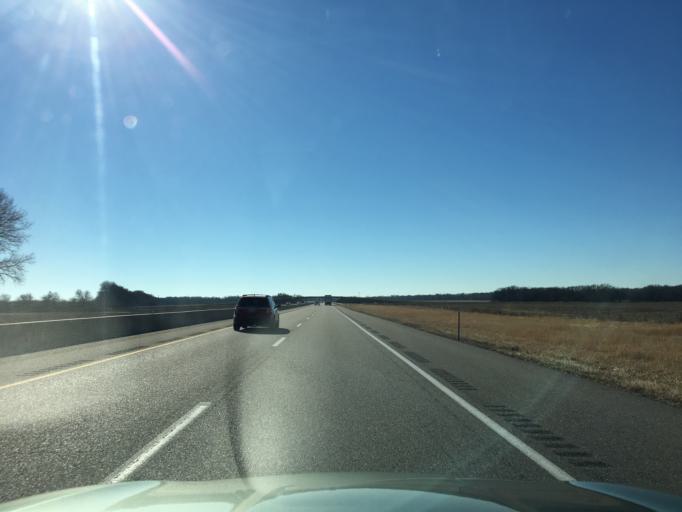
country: US
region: Kansas
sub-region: Sumner County
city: Belle Plaine
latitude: 37.4126
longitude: -97.3221
